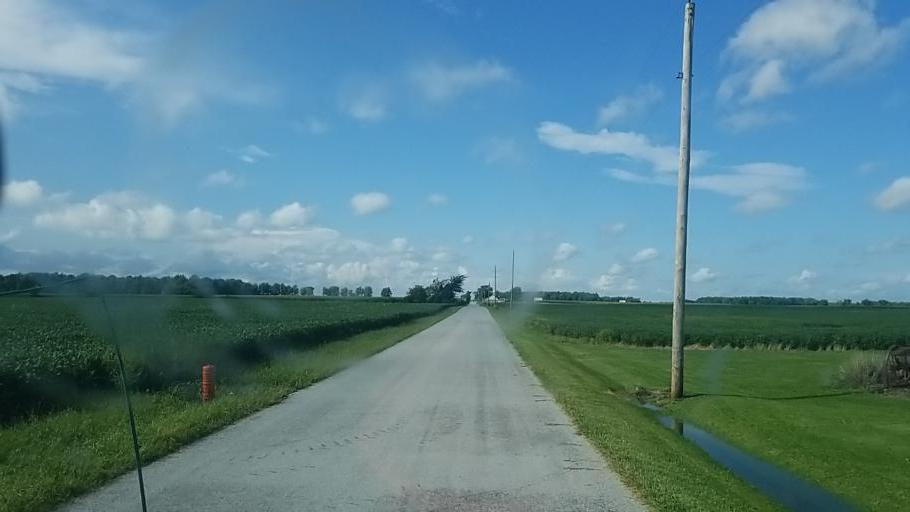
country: US
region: Ohio
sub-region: Hardin County
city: Kenton
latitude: 40.6760
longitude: -83.5310
